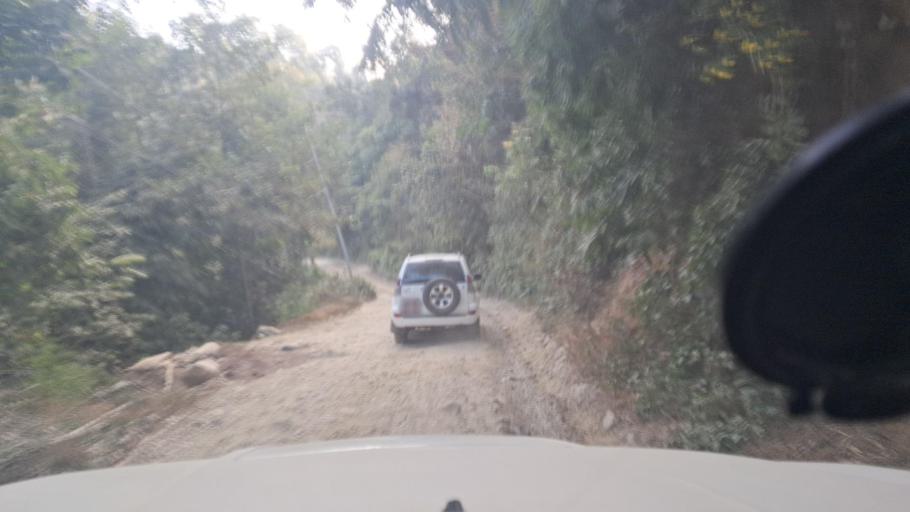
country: NP
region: Central Region
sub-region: Bagmati Zone
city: Patan
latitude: 27.5790
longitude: 85.3098
